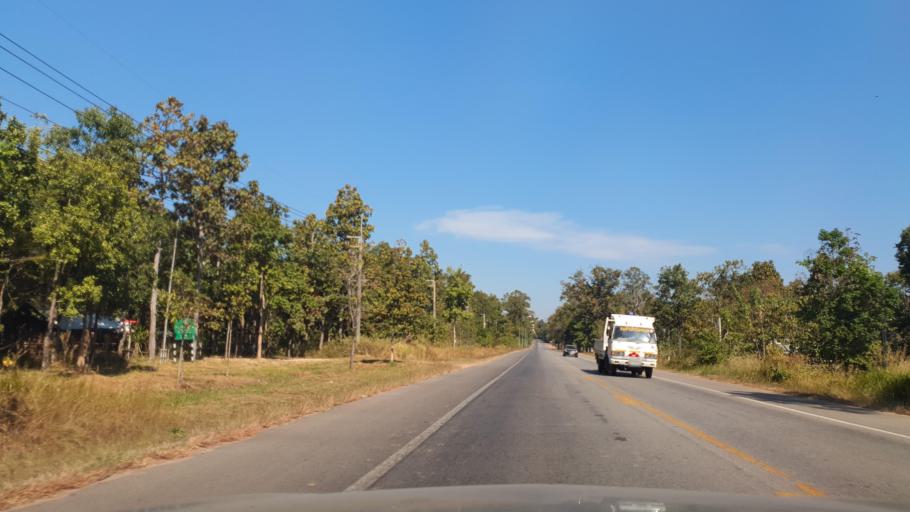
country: TH
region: Sakon Nakhon
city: Phu Phan
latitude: 17.0945
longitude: 103.9866
